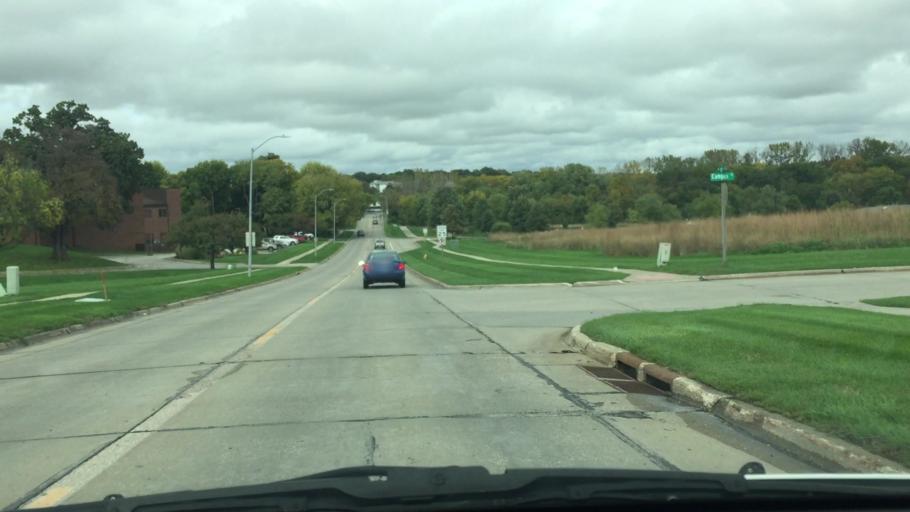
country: US
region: Iowa
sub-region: Polk County
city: Clive
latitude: 41.6070
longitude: -93.7749
